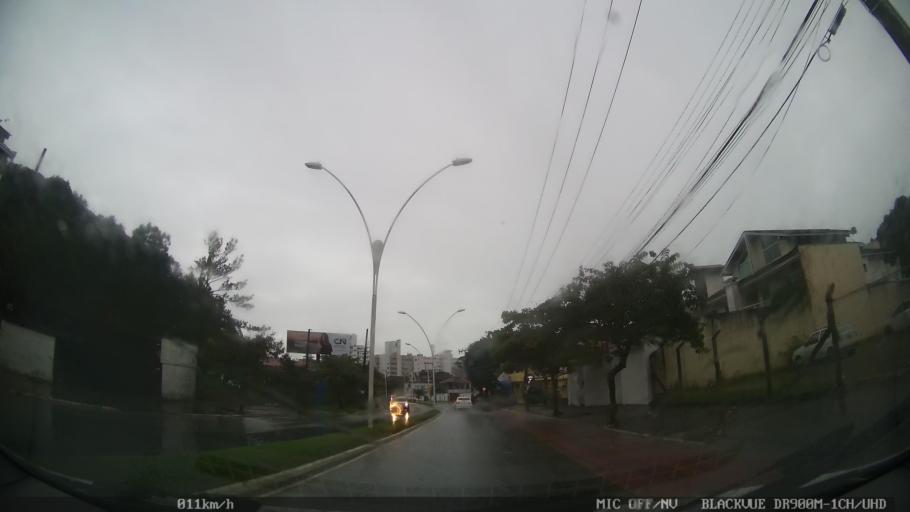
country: BR
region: Santa Catarina
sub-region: Balneario Camboriu
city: Balneario Camboriu
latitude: -26.9612
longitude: -48.6312
